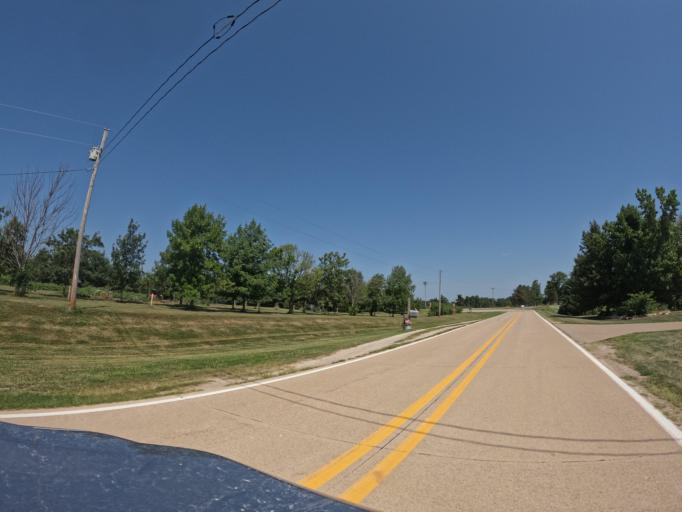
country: US
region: Iowa
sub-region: Henry County
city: Mount Pleasant
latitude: 40.8848
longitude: -91.5603
